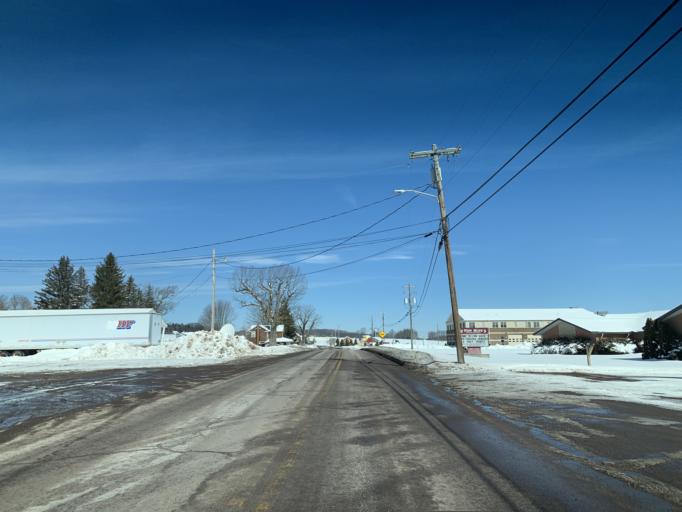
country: US
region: Pennsylvania
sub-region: Somerset County
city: Meyersdale
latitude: 39.7002
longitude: -79.1617
